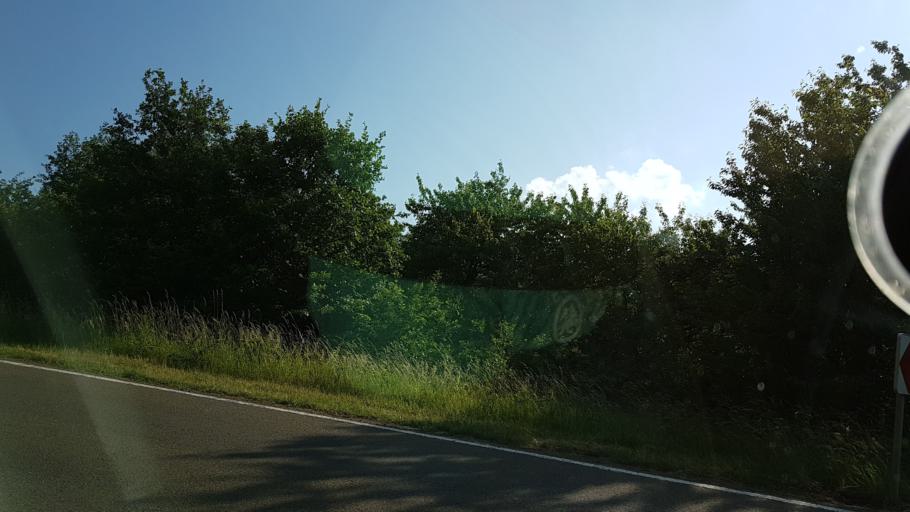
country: DE
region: Rheinland-Pfalz
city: Unkenbach
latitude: 49.7106
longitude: 7.7424
